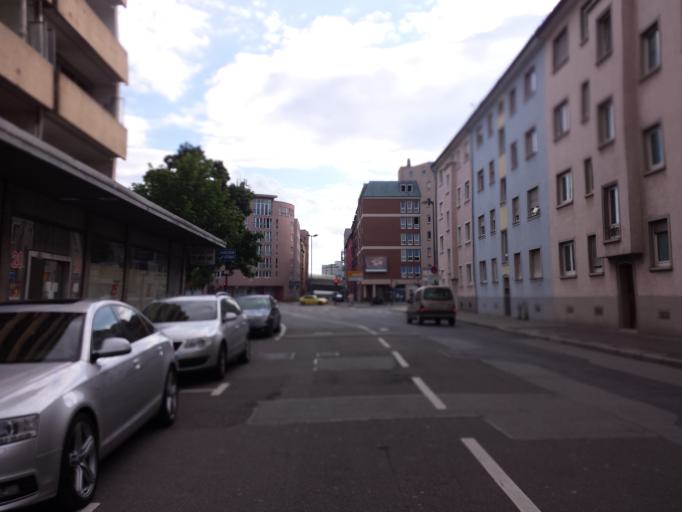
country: DE
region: Rheinland-Pfalz
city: Ludwigshafen am Rhein
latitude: 49.4785
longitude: 8.4458
